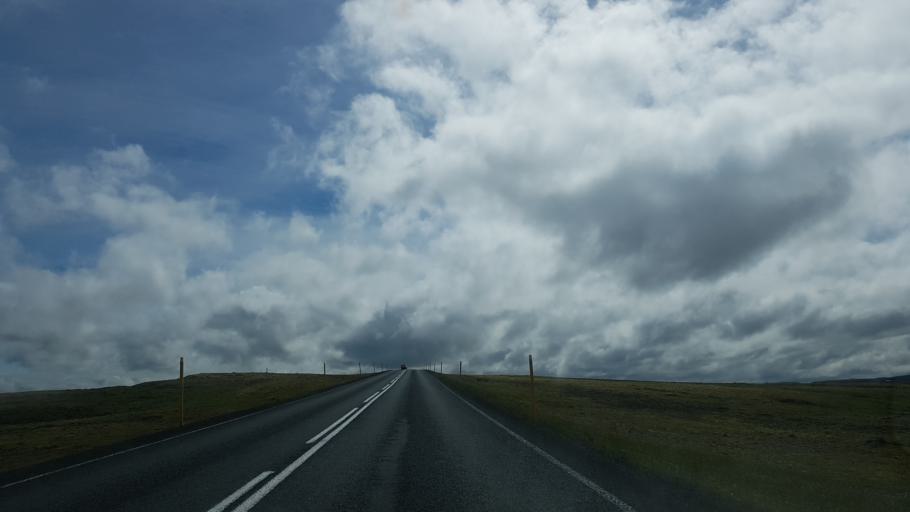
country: IS
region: West
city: Borgarnes
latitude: 65.0121
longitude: -21.0682
